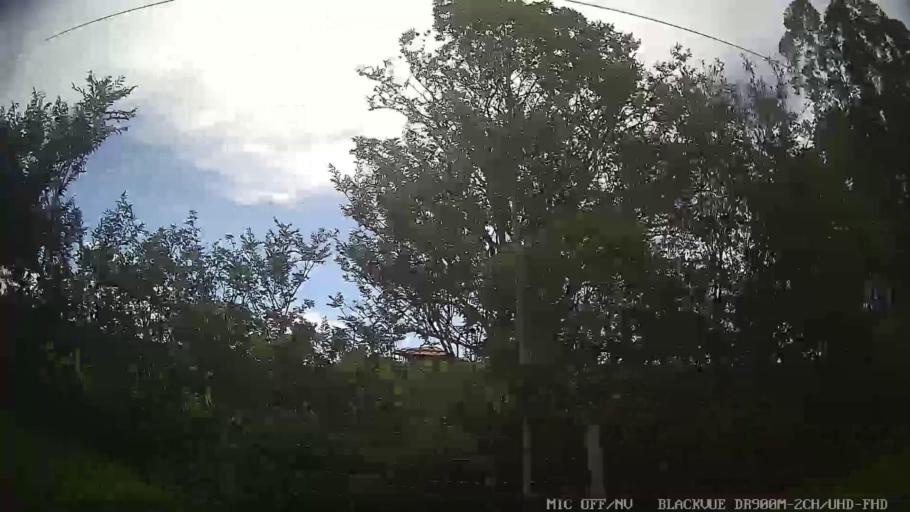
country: BR
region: Sao Paulo
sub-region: Conchas
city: Conchas
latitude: -22.9844
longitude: -47.9910
